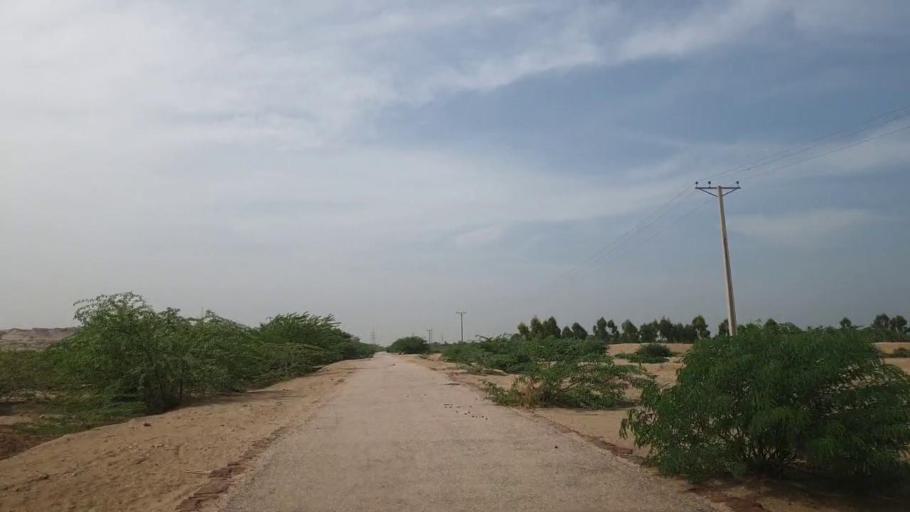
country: PK
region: Sindh
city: Kot Diji
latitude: 27.3702
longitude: 68.7651
